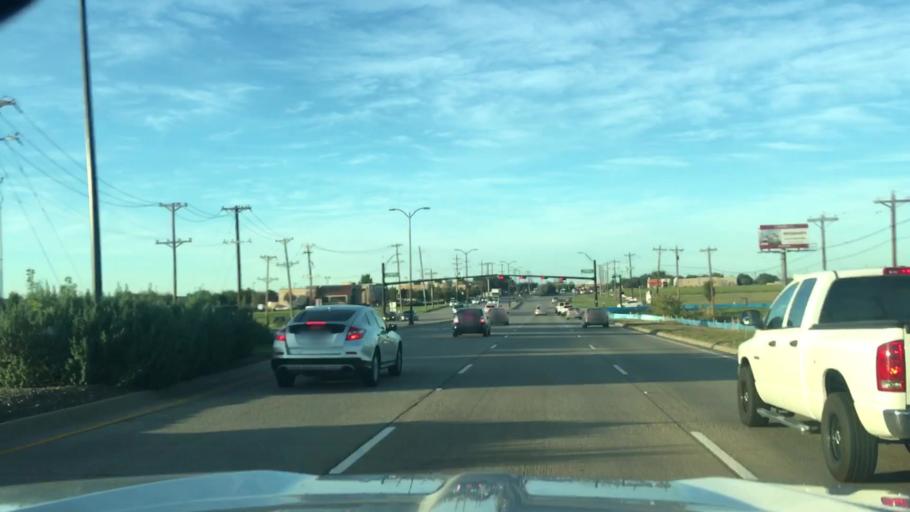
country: US
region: Texas
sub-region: Collin County
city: Frisco
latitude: 33.1443
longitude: -96.8046
